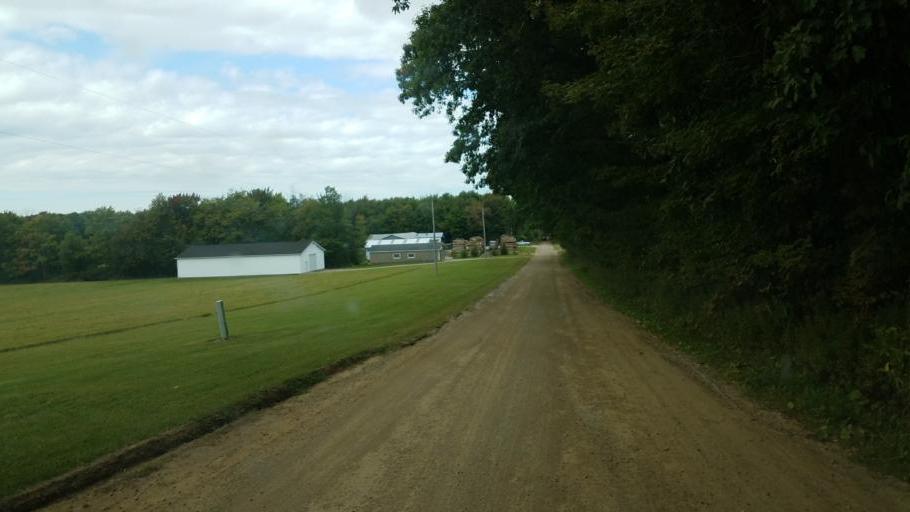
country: US
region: Pennsylvania
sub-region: Mercer County
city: Greenville
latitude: 41.4842
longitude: -80.3150
